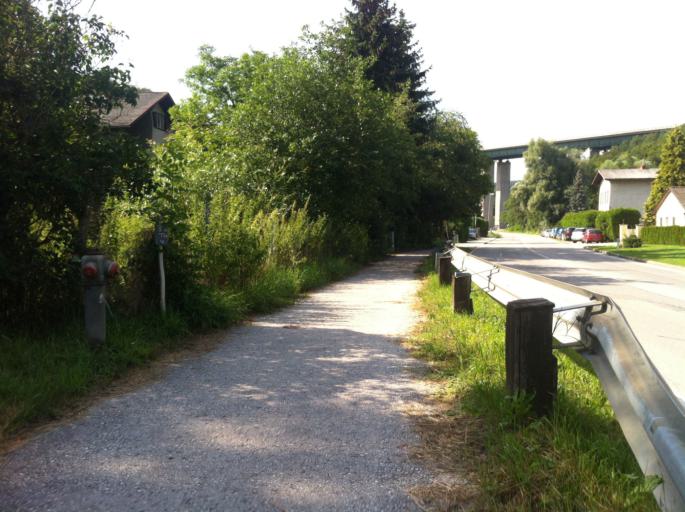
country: AT
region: Lower Austria
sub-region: Politischer Bezirk Wien-Umgebung
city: Wolfsgraben
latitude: 48.1716
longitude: 16.1245
